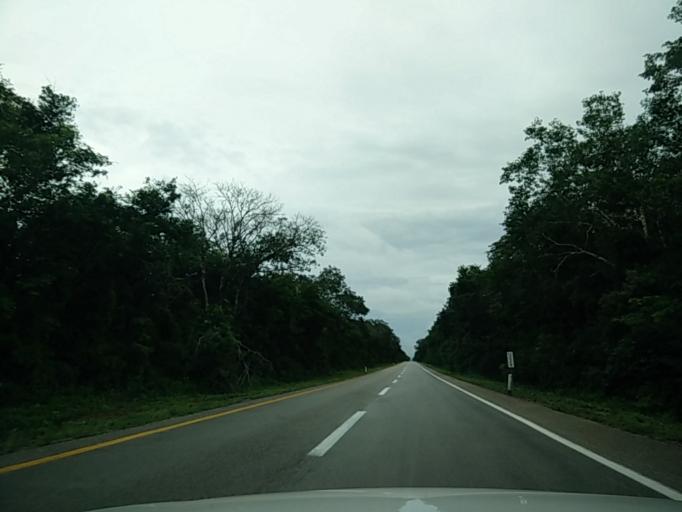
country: MX
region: Quintana Roo
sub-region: Lazaro Cardenas
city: Ignacio Zaragoza
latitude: 20.8919
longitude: -87.5206
